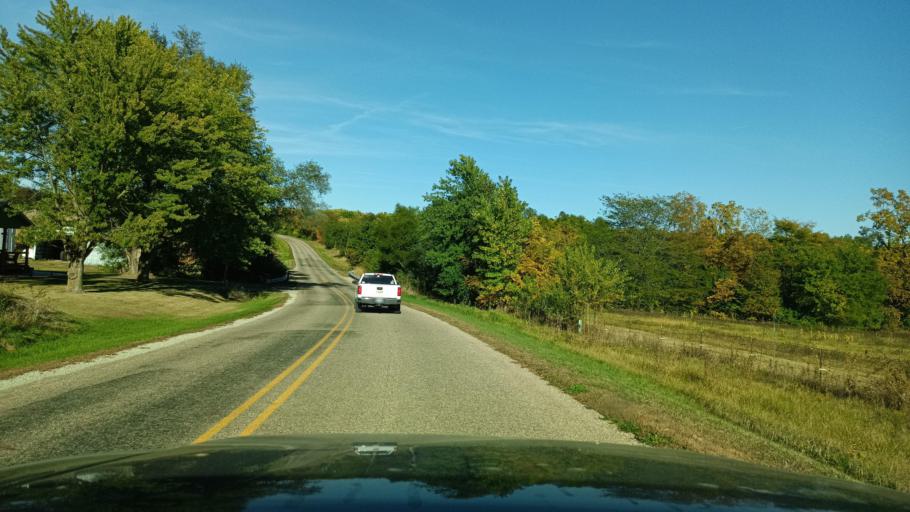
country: US
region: Illinois
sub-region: Logan County
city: Atlanta
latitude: 40.2346
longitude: -89.1322
